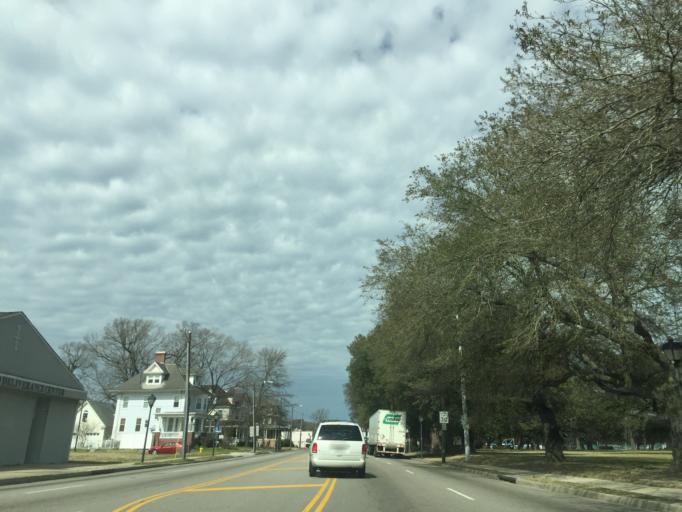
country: US
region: Virginia
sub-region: City of Norfolk
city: Norfolk
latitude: 36.8764
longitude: -76.2817
